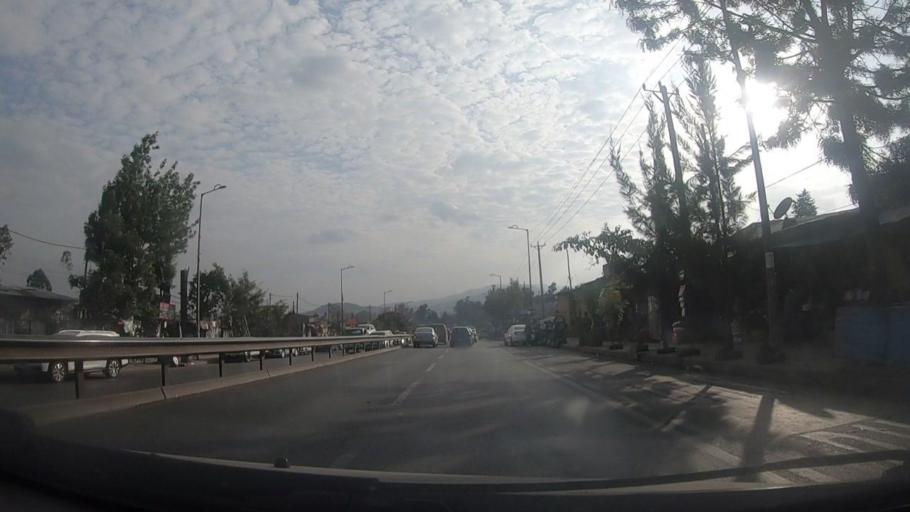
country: ET
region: Adis Abeba
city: Addis Ababa
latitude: 8.9802
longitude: 38.7345
